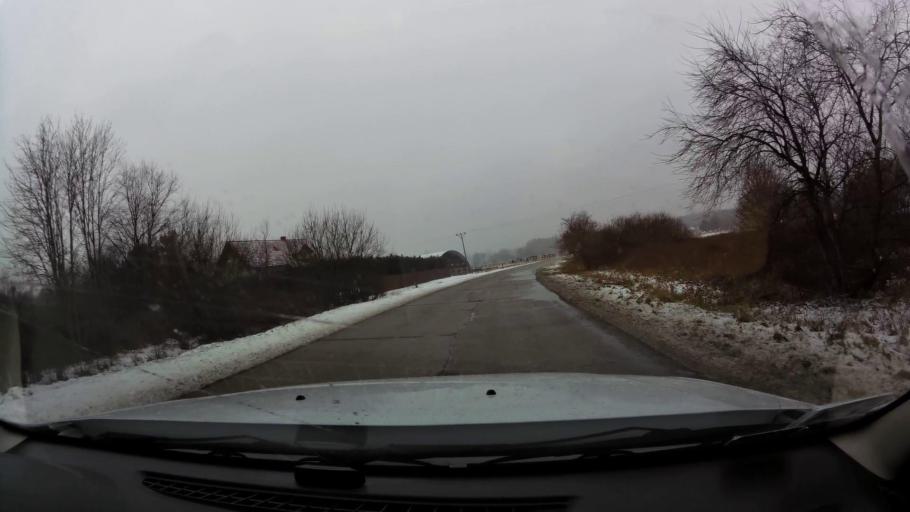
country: PL
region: West Pomeranian Voivodeship
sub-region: Powiat gryficki
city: Mrzezyno
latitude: 54.1412
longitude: 15.2931
